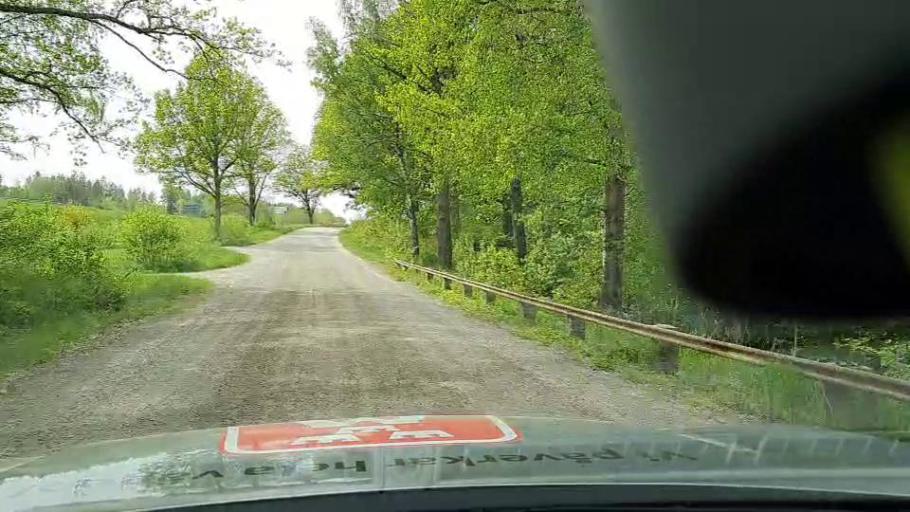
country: SE
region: Soedermanland
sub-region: Flens Kommun
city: Flen
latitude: 59.0381
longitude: 16.5767
